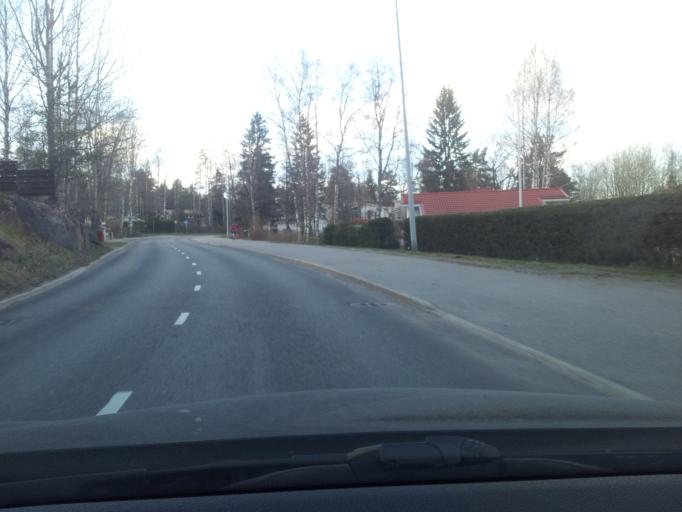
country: FI
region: Uusimaa
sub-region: Helsinki
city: Espoo
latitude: 60.1419
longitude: 24.6835
